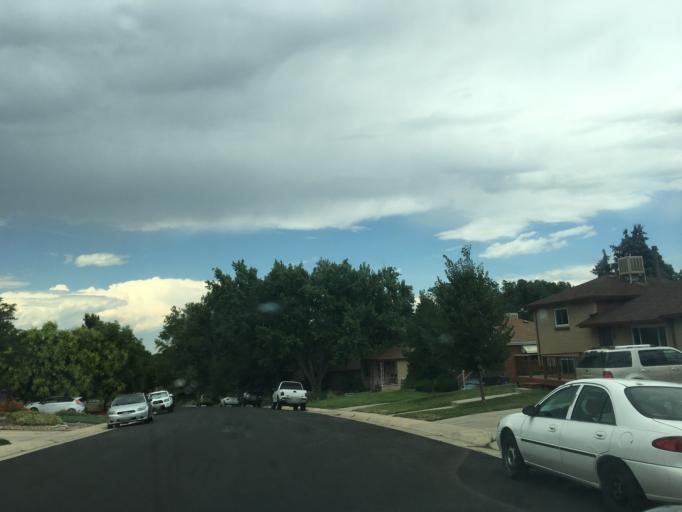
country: US
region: Colorado
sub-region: Arapahoe County
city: Sheridan
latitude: 39.6752
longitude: -105.0489
